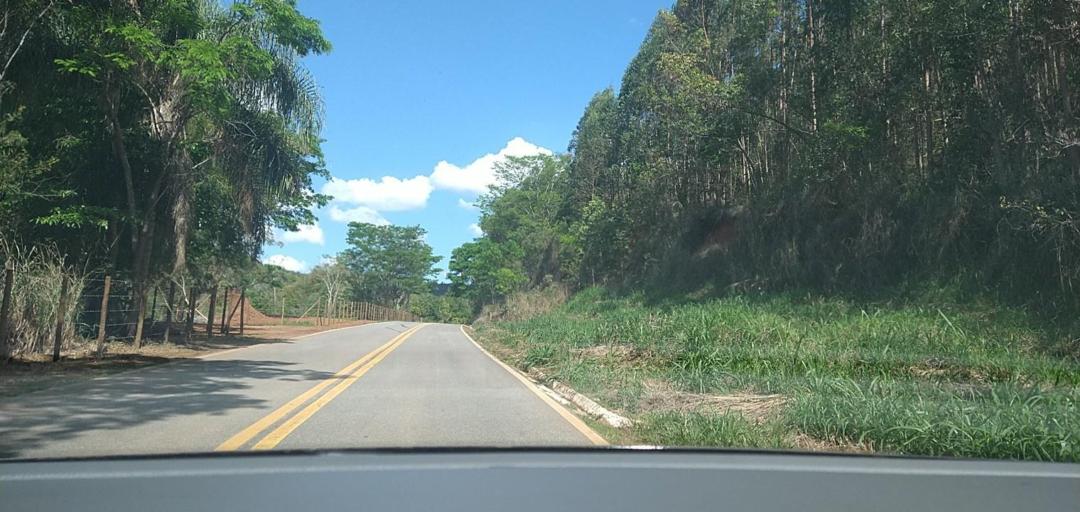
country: BR
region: Minas Gerais
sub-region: Rio Piracicaba
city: Rio Piracicaba
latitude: -19.9536
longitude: -43.1676
